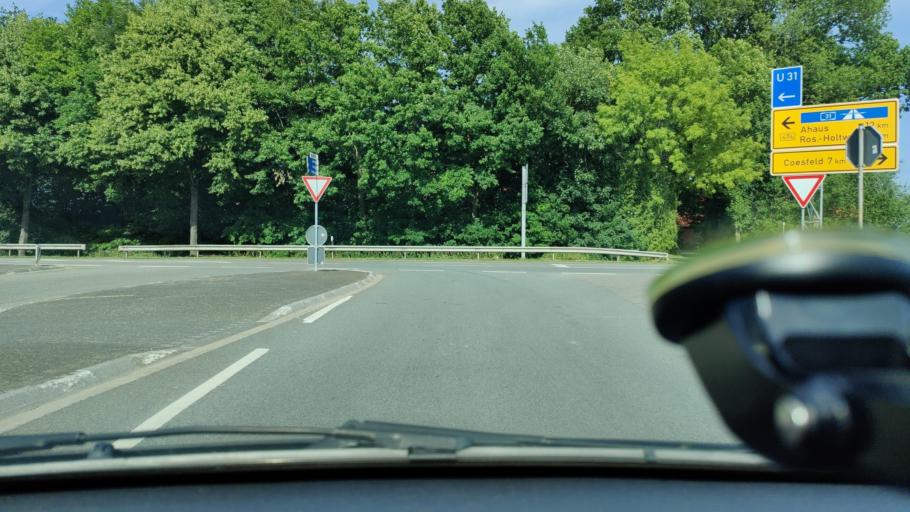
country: DE
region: North Rhine-Westphalia
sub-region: Regierungsbezirk Munster
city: Legden
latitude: 52.0004
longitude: 7.1280
